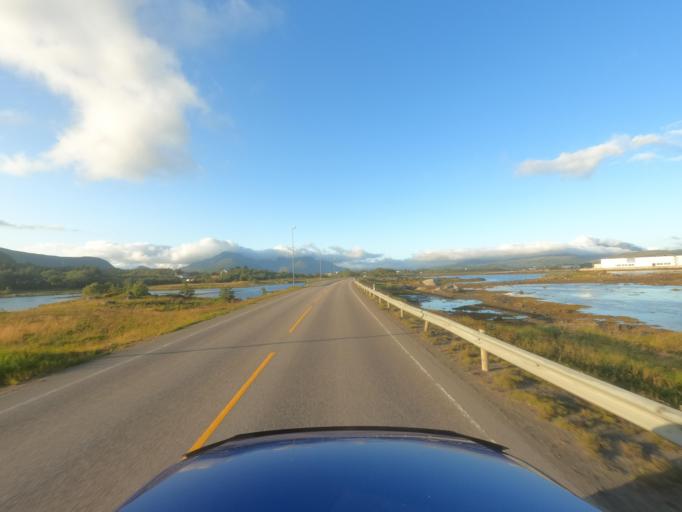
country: NO
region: Nordland
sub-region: Vestvagoy
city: Gravdal
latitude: 68.1273
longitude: 13.5506
